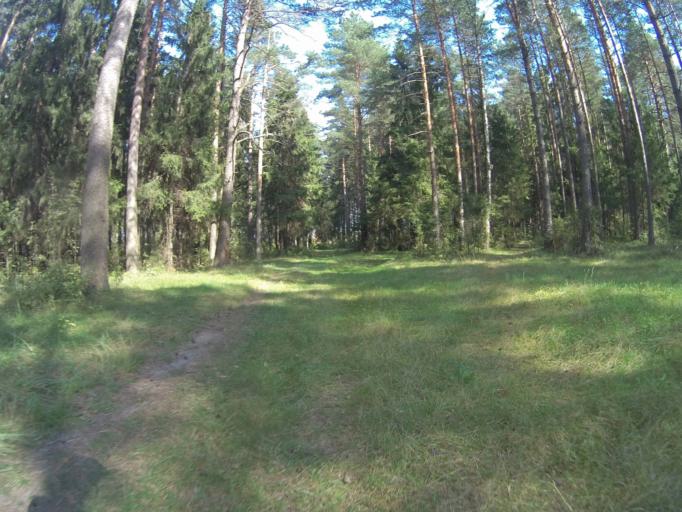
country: RU
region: Vladimir
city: Kommunar
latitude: 56.1056
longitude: 40.5227
